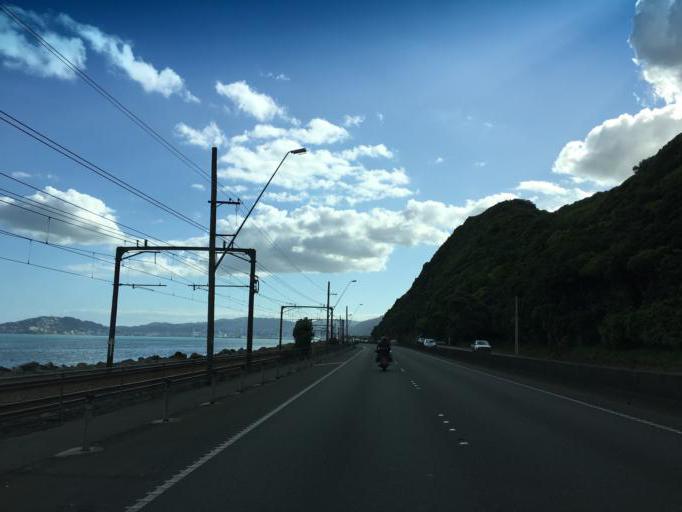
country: NZ
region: Wellington
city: Petone
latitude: -41.2380
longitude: 174.8294
